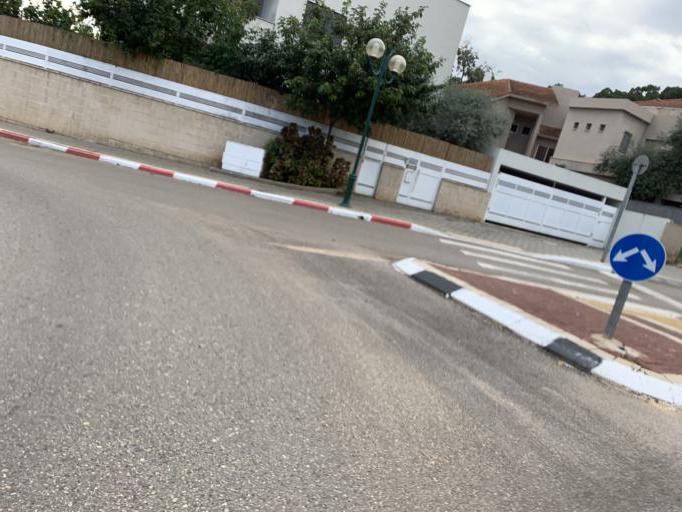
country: IL
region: Central District
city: Hod HaSharon
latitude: 32.1561
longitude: 34.8869
